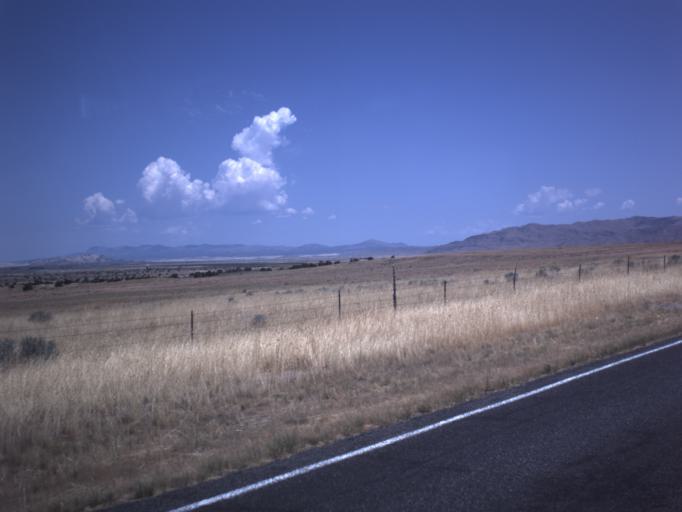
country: US
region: Utah
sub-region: Millard County
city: Delta
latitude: 39.4426
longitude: -112.3139
